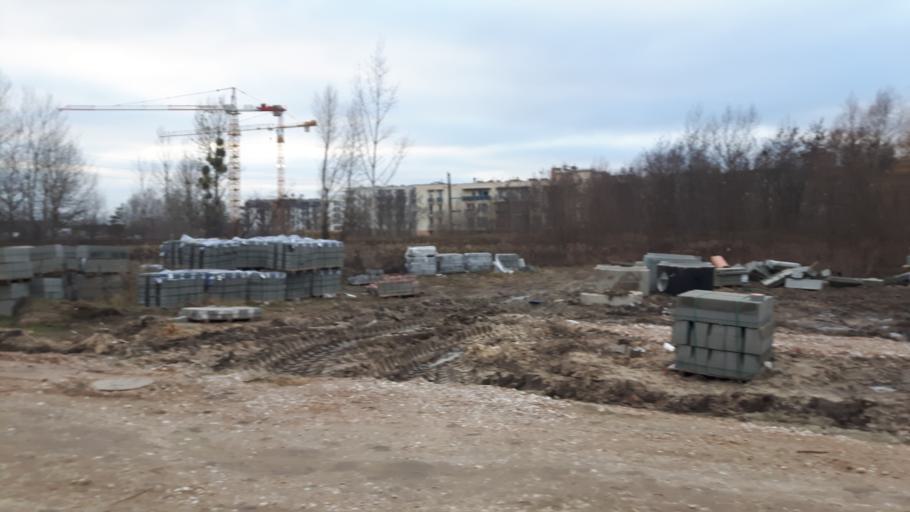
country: PL
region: Masovian Voivodeship
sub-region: Powiat wolominski
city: Zabki
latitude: 52.2767
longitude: 21.1224
